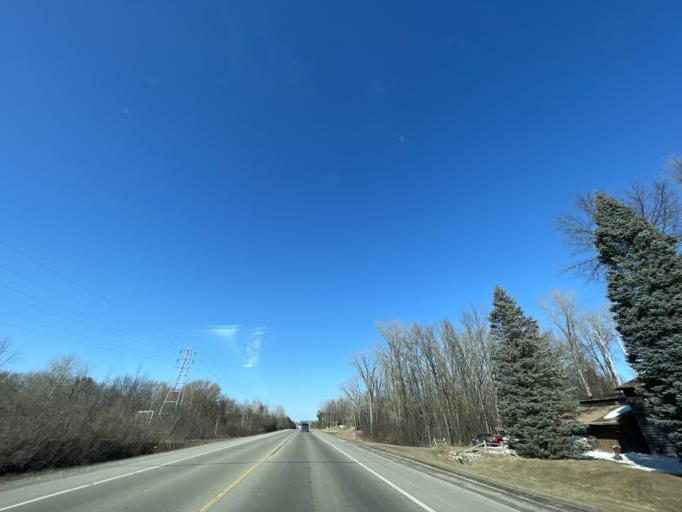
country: US
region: Wisconsin
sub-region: Brown County
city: Howard
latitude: 44.5950
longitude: -88.0779
